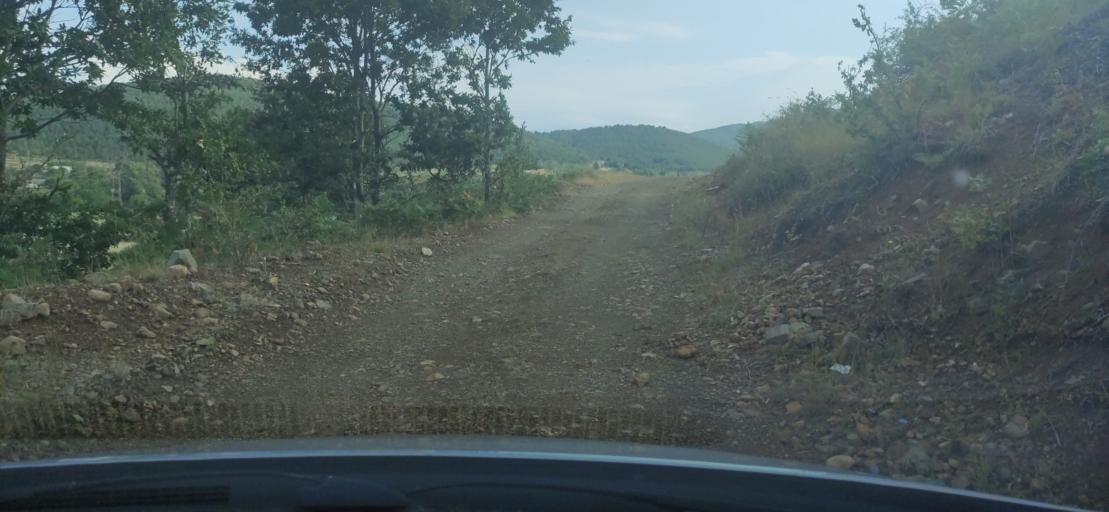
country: AL
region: Shkoder
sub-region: Rrethi i Pukes
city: Iballe
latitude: 42.1851
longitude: 19.9961
